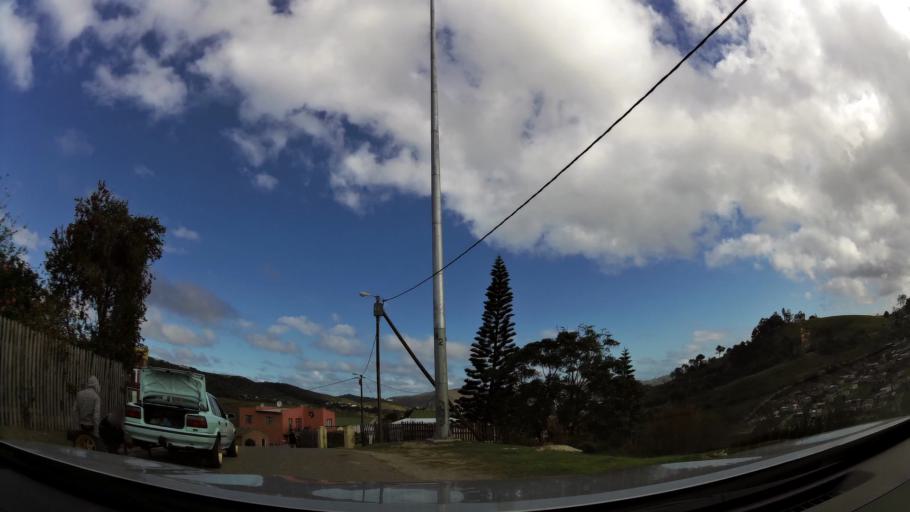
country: ZA
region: Western Cape
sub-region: Eden District Municipality
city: Knysna
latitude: -34.0531
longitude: 23.0945
